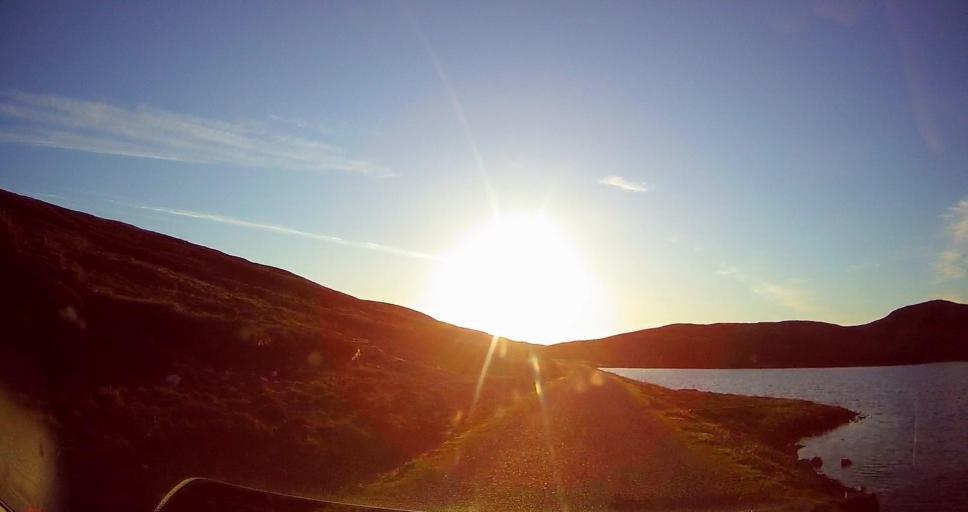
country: GB
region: Scotland
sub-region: Shetland Islands
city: Lerwick
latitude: 60.4432
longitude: -1.4071
